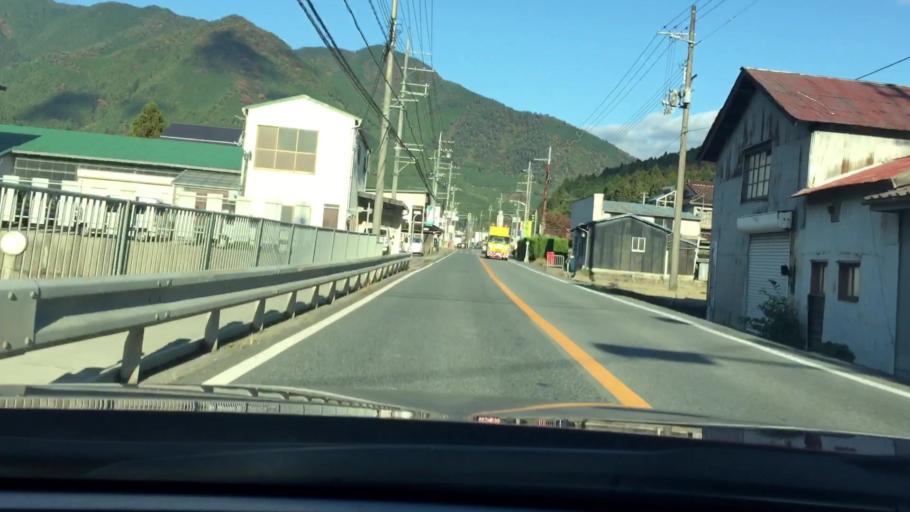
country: JP
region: Hyogo
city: Yamazakicho-nakabirose
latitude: 35.1090
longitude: 134.5787
